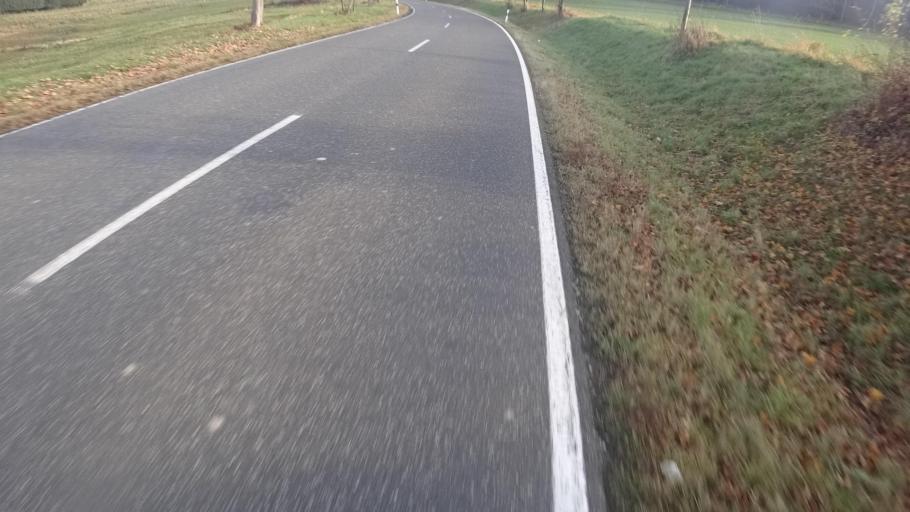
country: DE
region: Rheinland-Pfalz
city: Muhlpfad
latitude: 50.1166
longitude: 7.5659
